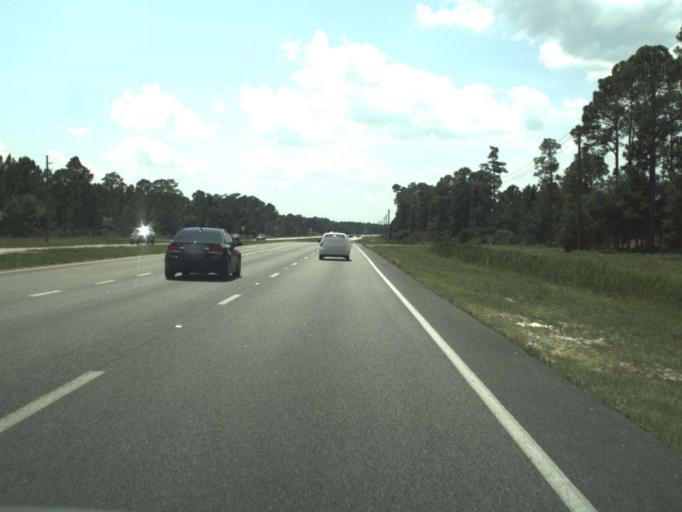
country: US
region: Florida
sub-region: Volusia County
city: Samsula-Spruce Creek
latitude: 29.0113
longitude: -81.0703
